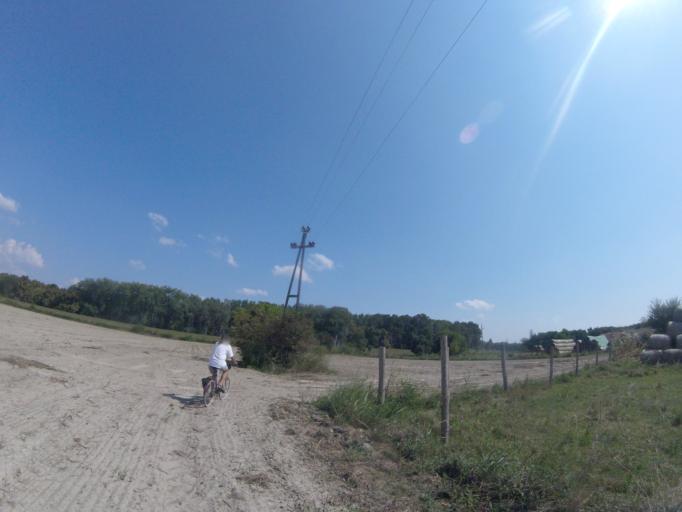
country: HU
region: Tolna
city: Bata
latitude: 46.2076
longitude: 18.8194
